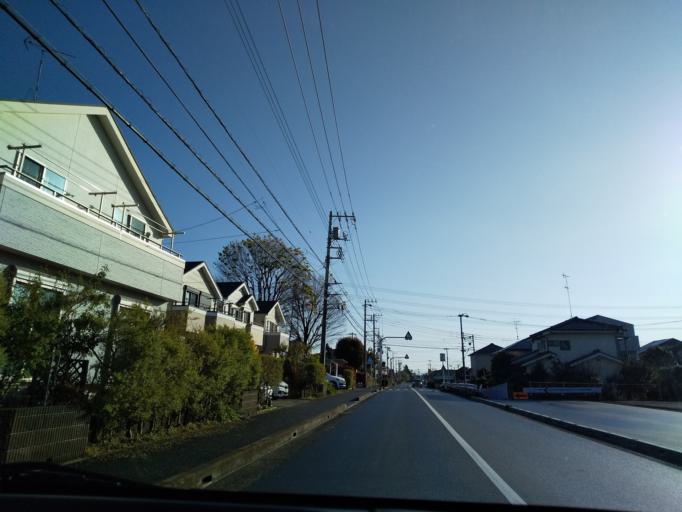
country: JP
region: Tokyo
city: Hino
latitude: 35.6515
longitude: 139.3746
